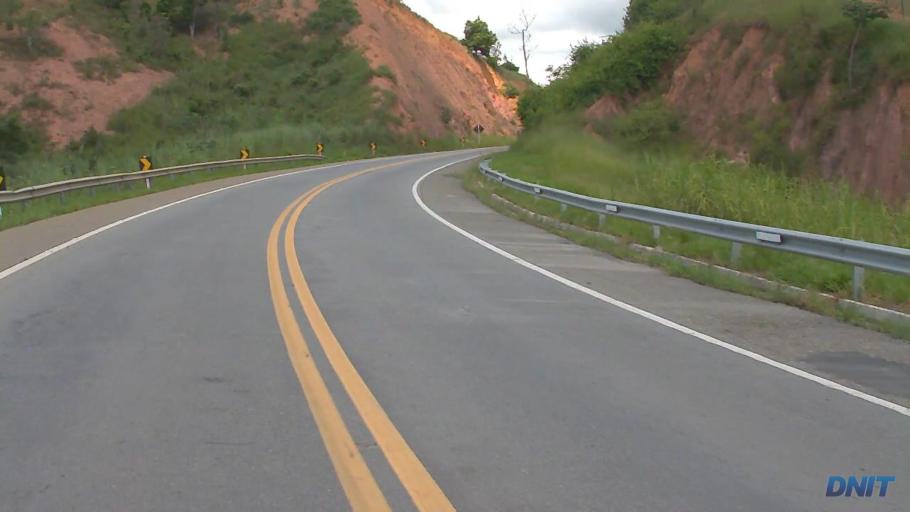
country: BR
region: Minas Gerais
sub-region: Belo Oriente
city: Belo Oriente
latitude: -19.0952
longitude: -42.1953
